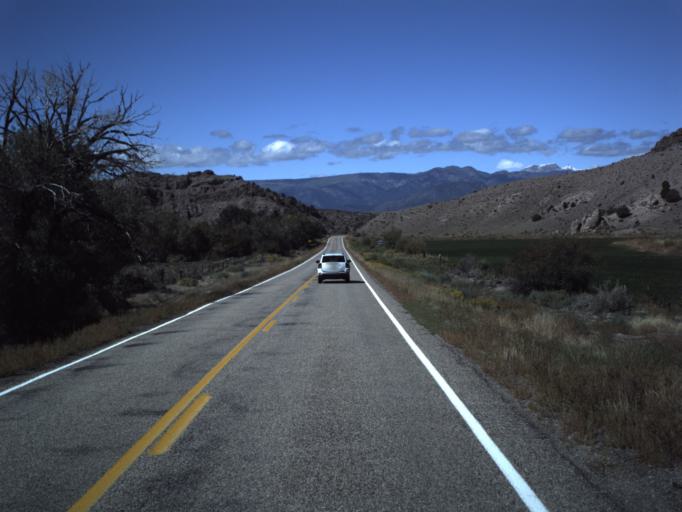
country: US
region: Utah
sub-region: Piute County
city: Junction
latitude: 38.1954
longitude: -112.1451
